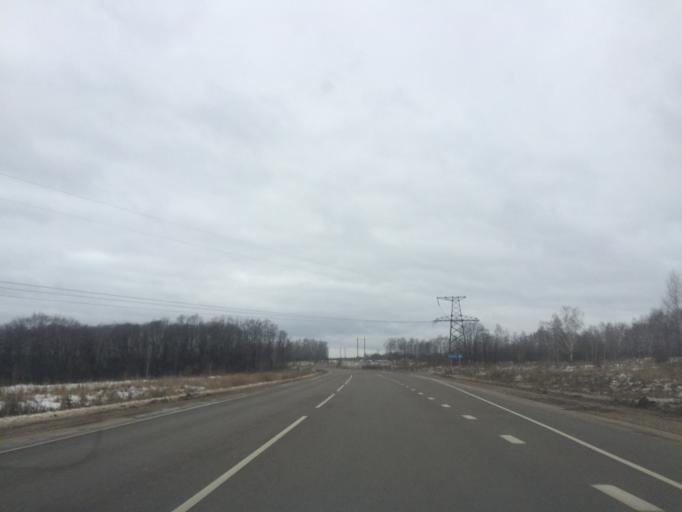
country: RU
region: Tula
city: Kosaya Gora
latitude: 54.1521
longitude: 37.4196
